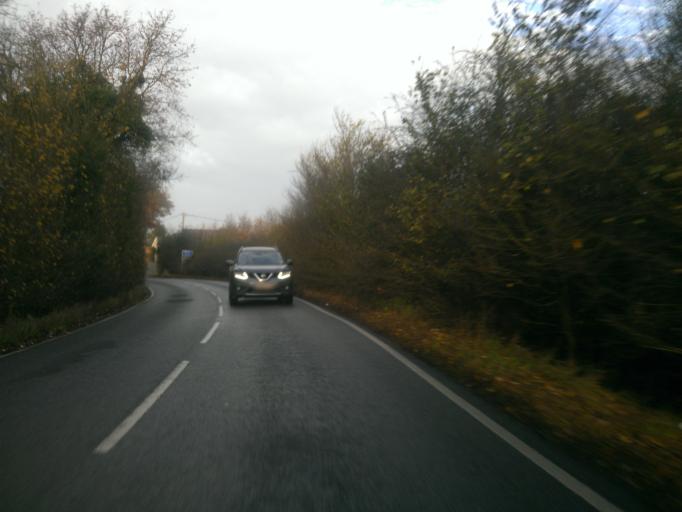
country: GB
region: England
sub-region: Essex
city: Wivenhoe
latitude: 51.8600
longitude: 0.9751
